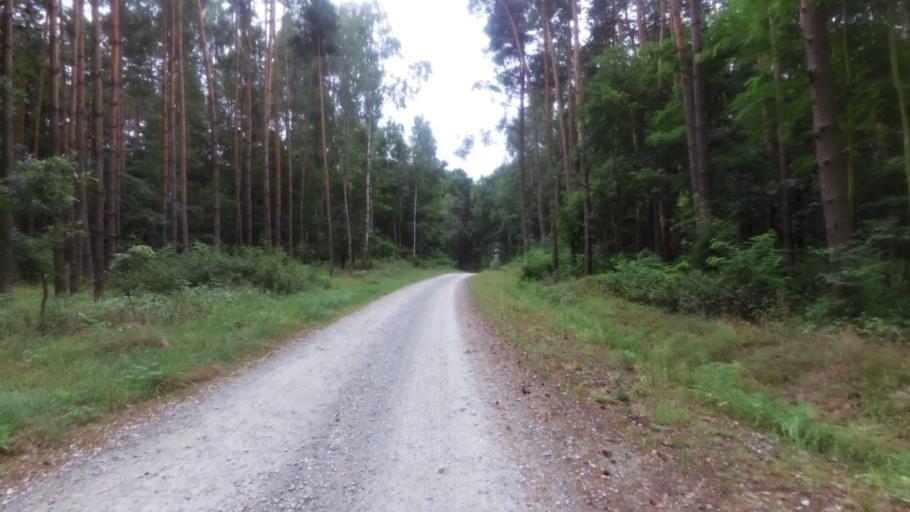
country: PL
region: Lubusz
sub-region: Powiat gorzowski
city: Kostrzyn nad Odra
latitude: 52.6591
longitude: 14.6351
